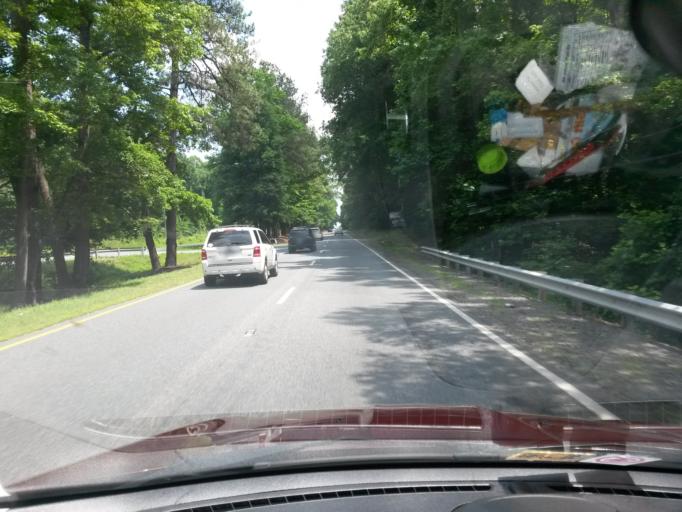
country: US
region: Virginia
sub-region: Chesterfield County
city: Enon
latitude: 37.3244
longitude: -77.3152
